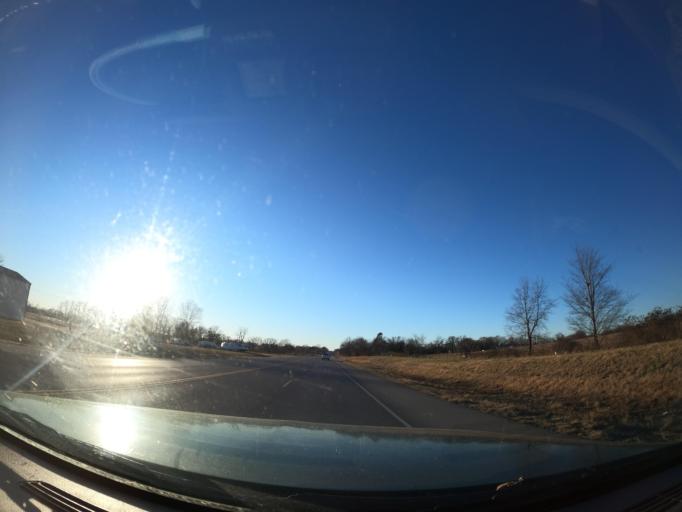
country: US
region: Oklahoma
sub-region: Pittsburg County
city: Krebs
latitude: 34.8940
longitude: -95.6370
